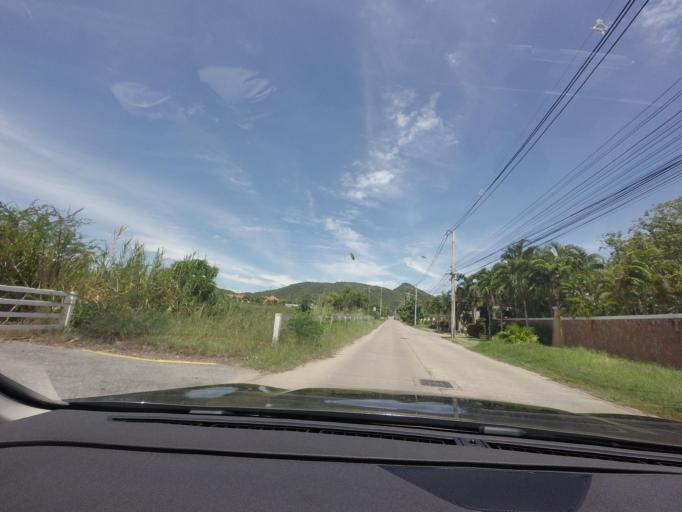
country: TH
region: Prachuap Khiri Khan
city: Hua Hin
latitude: 12.5135
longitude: 99.9702
